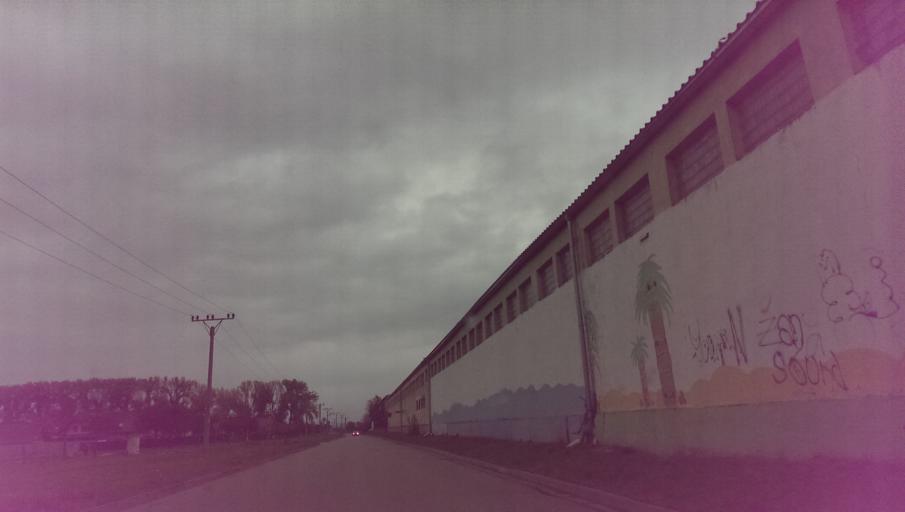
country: CZ
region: South Moravian
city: Pohorelice
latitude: 48.9827
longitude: 16.5130
